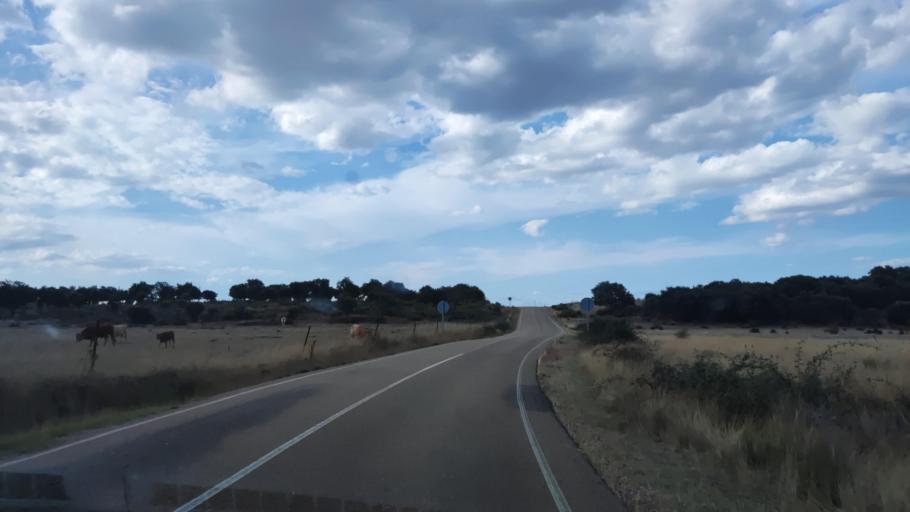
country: ES
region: Castille and Leon
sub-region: Provincia de Salamanca
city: Martiago
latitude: 40.4758
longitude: -6.4905
